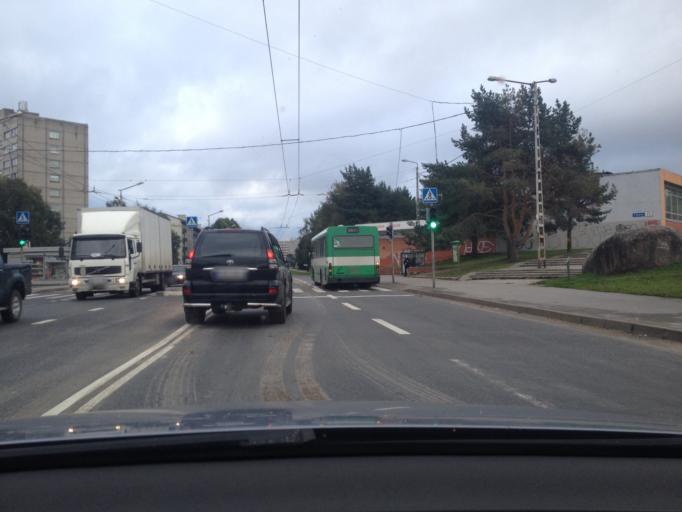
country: EE
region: Harju
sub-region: Tallinna linn
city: Tallinn
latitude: 59.4034
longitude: 24.6865
